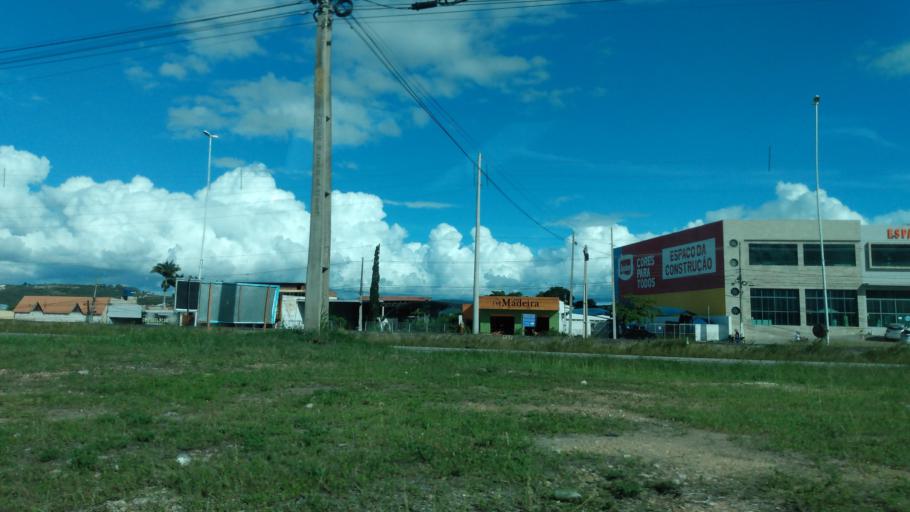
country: ET
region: Oromiya
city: Gore
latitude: 8.1947
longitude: 35.5640
